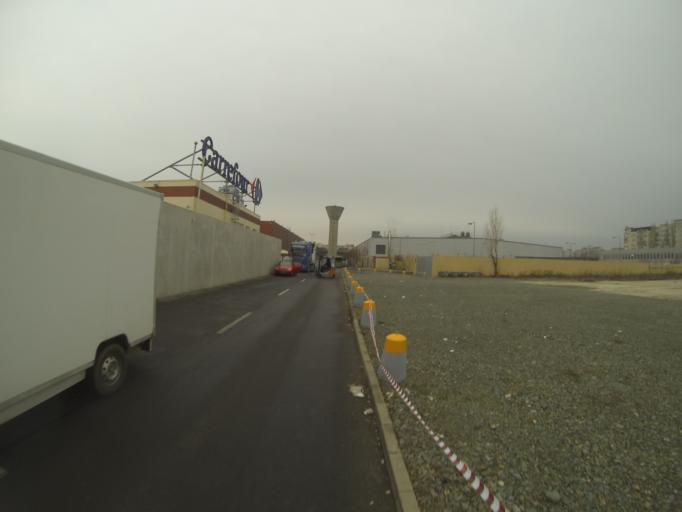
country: RO
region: Bucuresti
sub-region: Municipiul Bucuresti
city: Bucuresti
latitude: 44.4181
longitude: 26.0710
